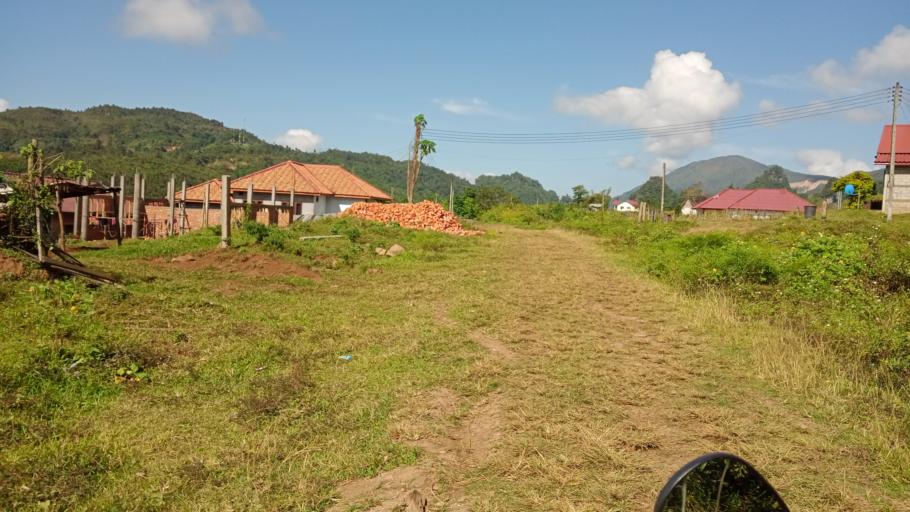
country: LA
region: Xiangkhoang
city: Phonsavan
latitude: 19.1038
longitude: 102.9336
